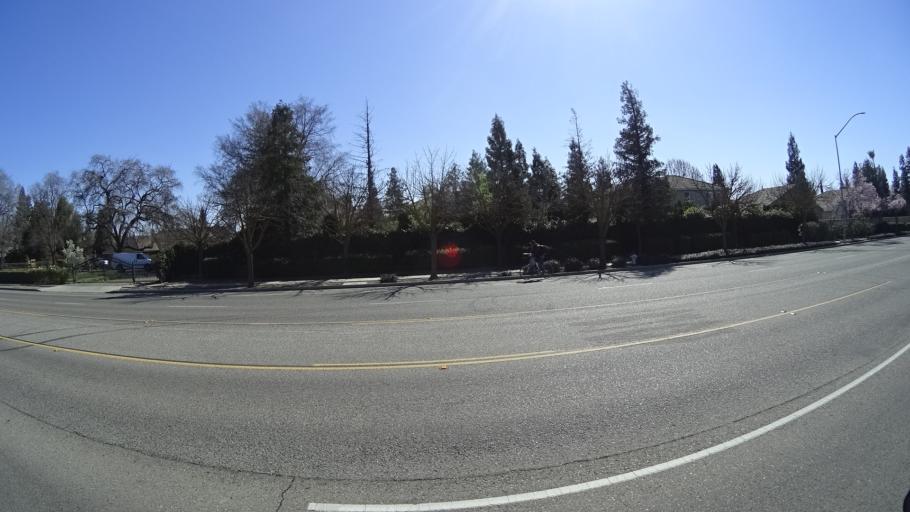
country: US
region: California
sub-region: Fresno County
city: Clovis
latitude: 36.8595
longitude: -119.7372
